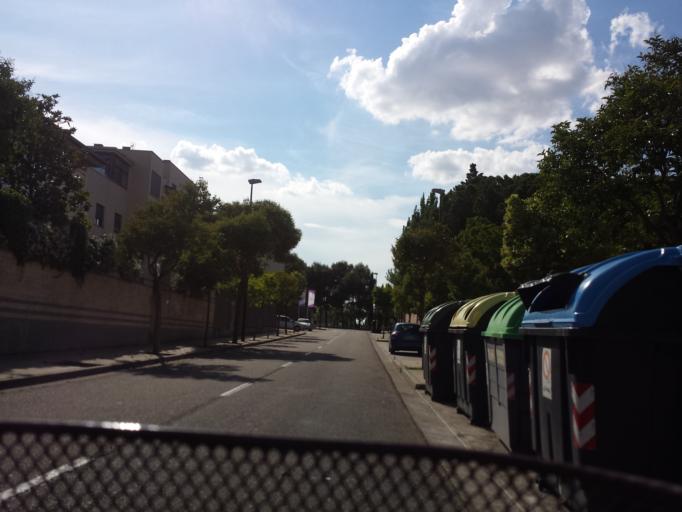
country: ES
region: Aragon
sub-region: Provincia de Zaragoza
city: Delicias
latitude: 41.6297
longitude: -0.9158
